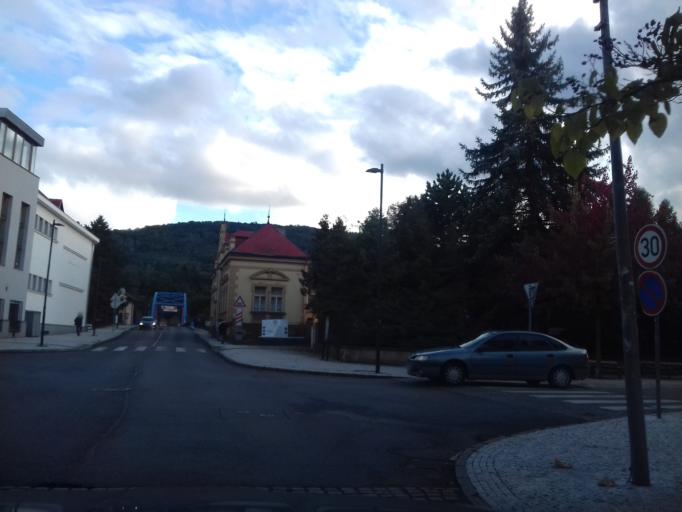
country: CZ
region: Central Bohemia
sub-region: Okres Praha-Zapad
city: Dobrichovice
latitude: 49.9272
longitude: 14.2747
